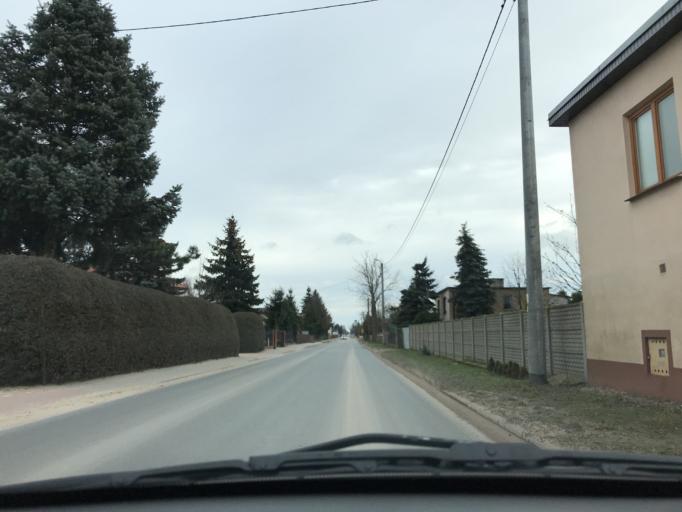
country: PL
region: Greater Poland Voivodeship
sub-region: Powiat poznanski
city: Baranowo
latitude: 52.4006
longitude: 16.7458
